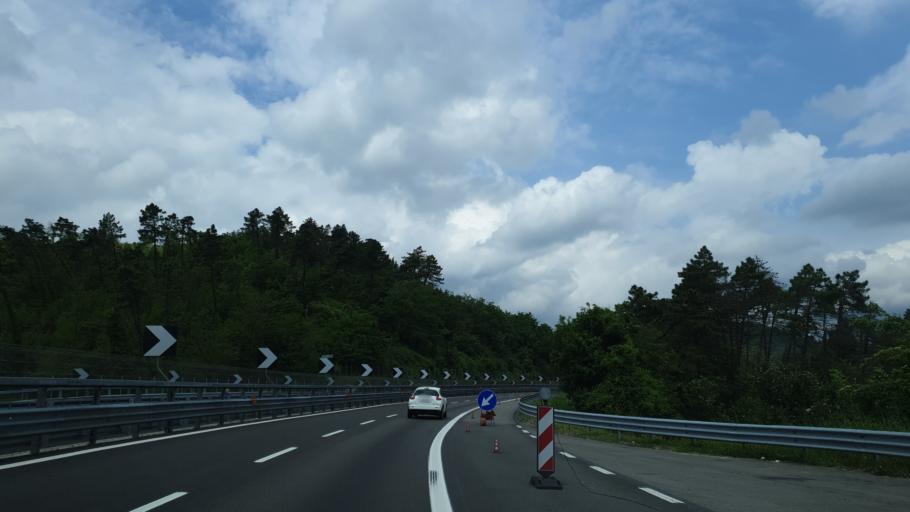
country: IT
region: Tuscany
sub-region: Province of Florence
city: Barberino di Mugello
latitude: 44.0073
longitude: 11.2188
